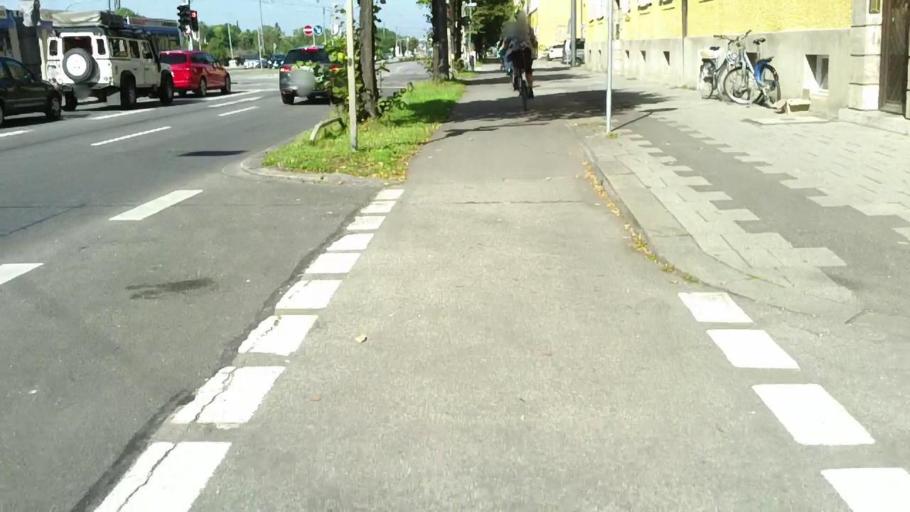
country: DE
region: Bavaria
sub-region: Upper Bavaria
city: Munich
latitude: 48.1696
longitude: 11.5336
